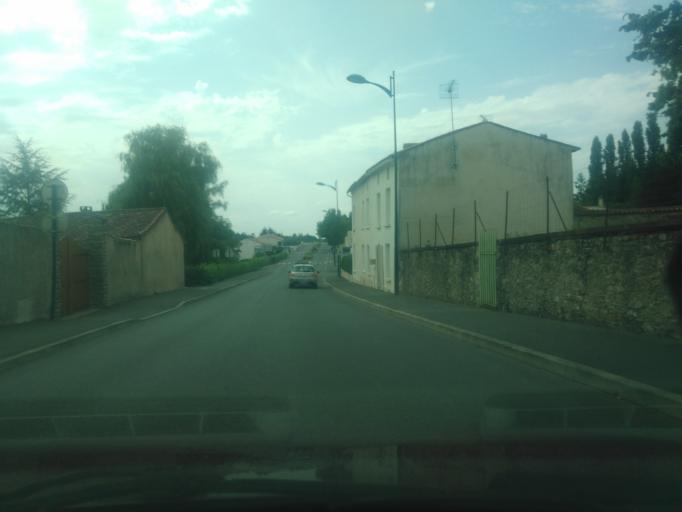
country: FR
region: Pays de la Loire
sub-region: Departement de la Vendee
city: La Chataigneraie
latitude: 46.6517
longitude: -0.7433
